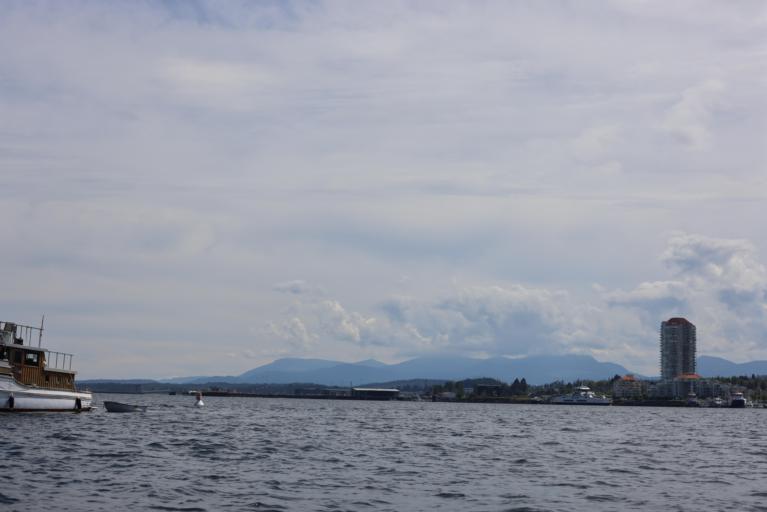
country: CA
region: British Columbia
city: Nanaimo
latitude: 49.1761
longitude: -123.9331
